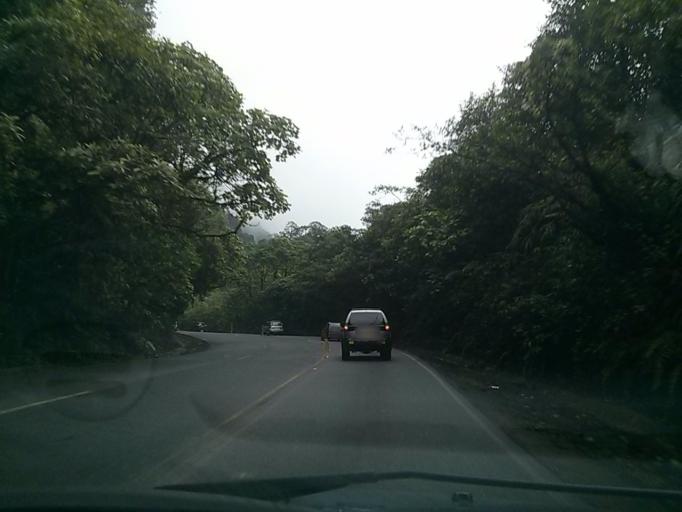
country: CR
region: San Jose
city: Dulce Nombre de Jesus
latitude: 10.0884
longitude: -83.9820
